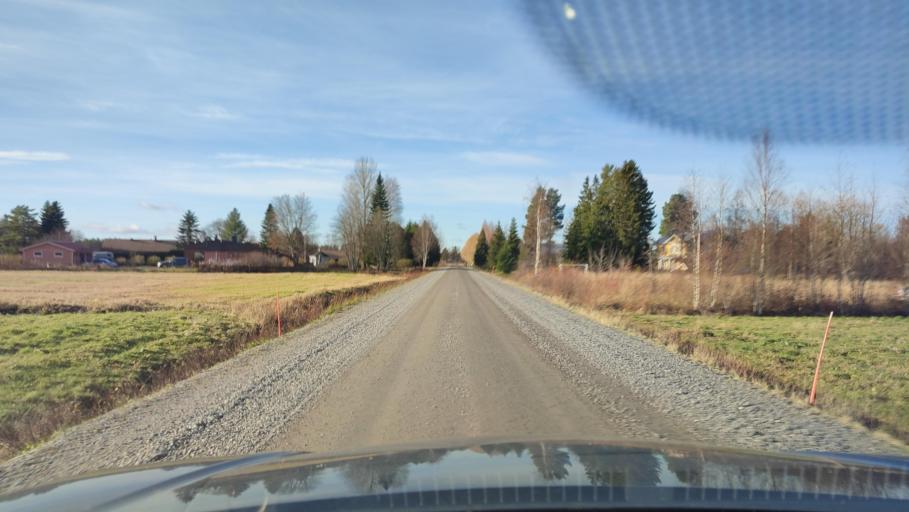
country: FI
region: Southern Ostrobothnia
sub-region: Suupohja
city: Teuva
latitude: 62.4565
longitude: 21.6337
